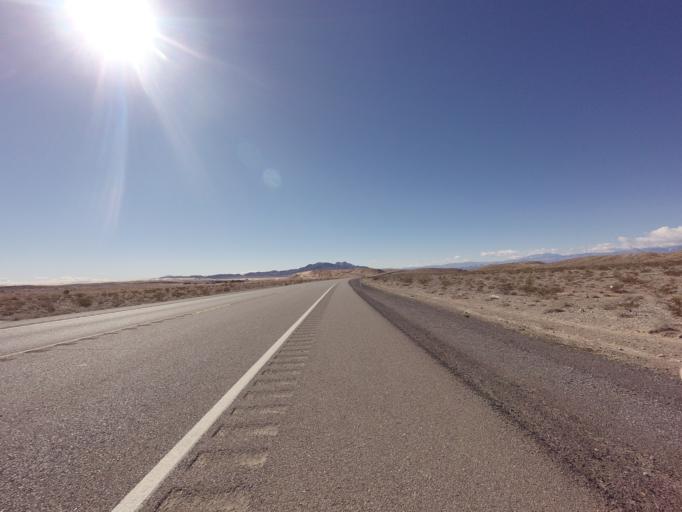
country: US
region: Nevada
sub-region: Clark County
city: Nellis Air Force Base
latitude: 36.3071
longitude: -114.9533
